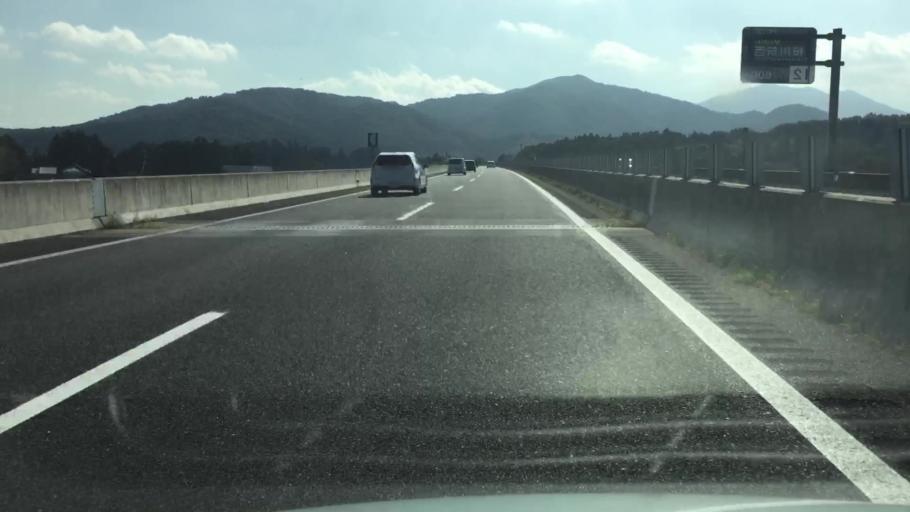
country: JP
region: Ibaraki
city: Iwase
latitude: 36.3567
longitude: 140.0895
